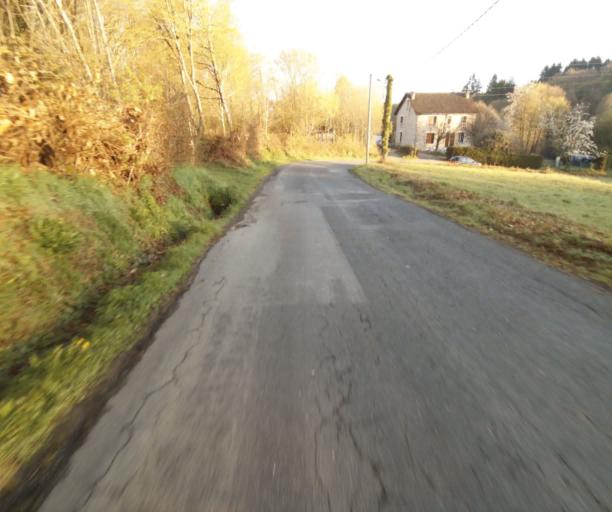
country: FR
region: Limousin
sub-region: Departement de la Correze
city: Naves
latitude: 45.3169
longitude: 1.8328
